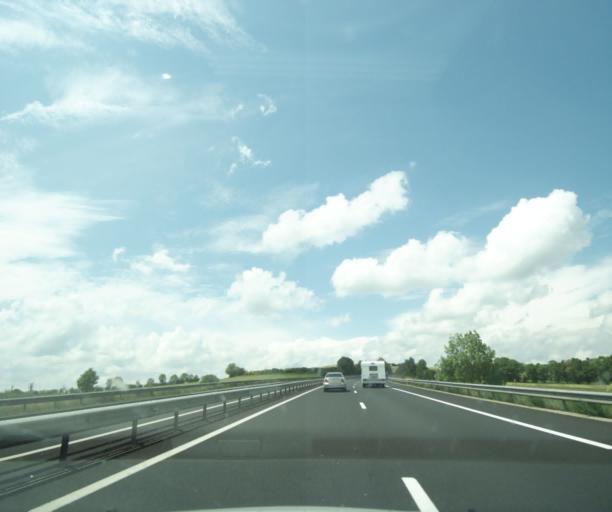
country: FR
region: Auvergne
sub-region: Departement du Cantal
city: Saint-Flour
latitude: 45.0370
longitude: 3.1246
